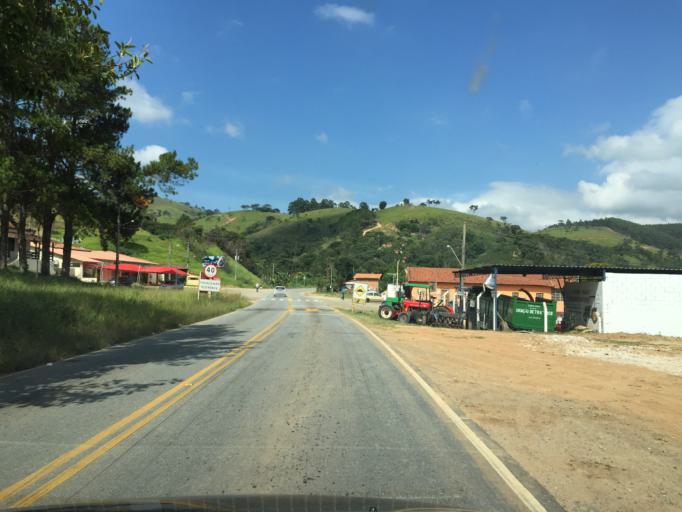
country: BR
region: Minas Gerais
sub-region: Passa Quatro
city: Passa Quatro
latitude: -22.3886
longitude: -44.9630
